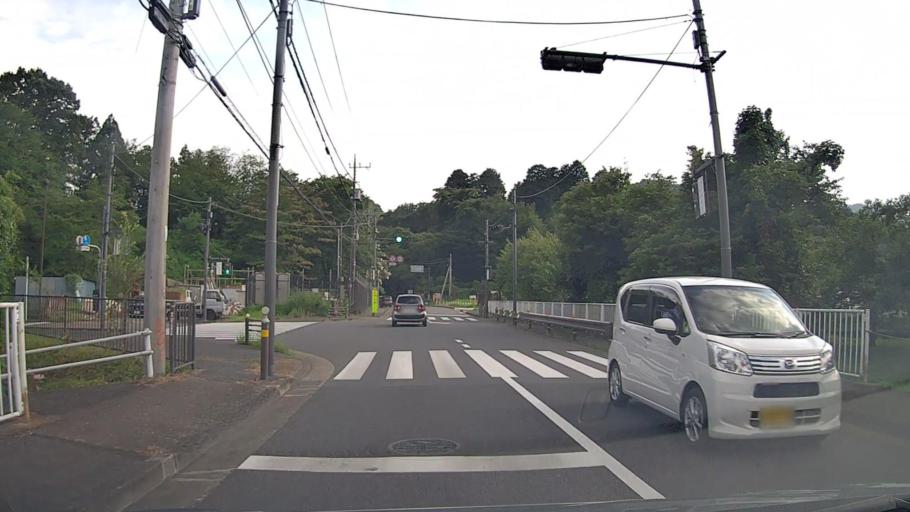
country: JP
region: Tokyo
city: Itsukaichi
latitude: 35.7218
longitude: 139.2319
